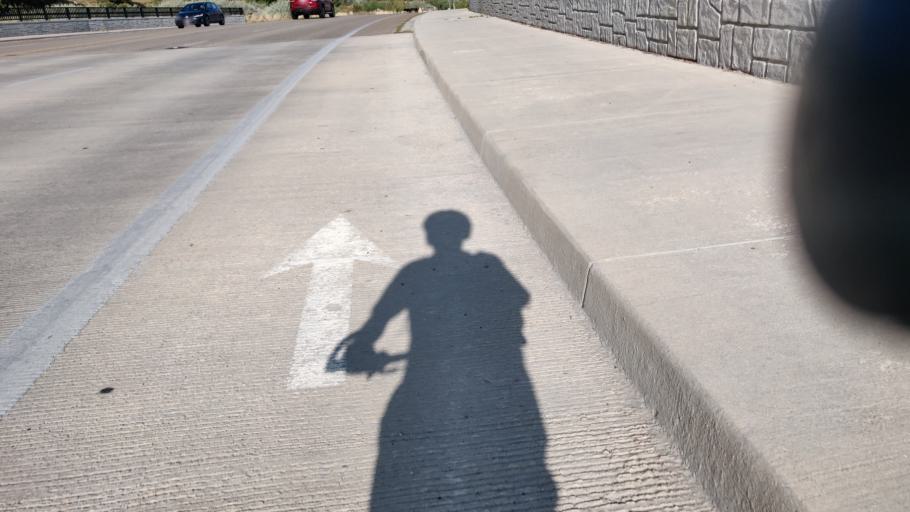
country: US
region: Idaho
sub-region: Ada County
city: Boise
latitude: 43.5778
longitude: -116.1474
